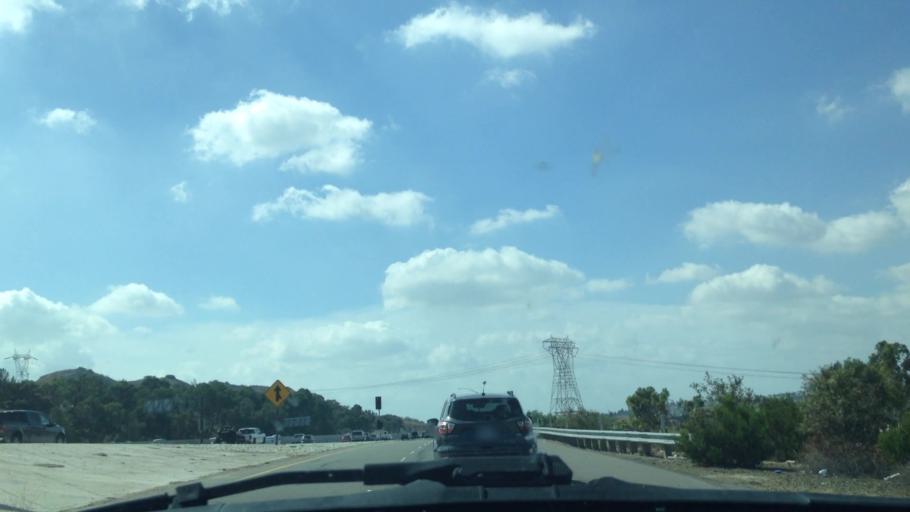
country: US
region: California
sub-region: Orange County
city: Yorba Linda
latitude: 33.8708
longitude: -117.7466
